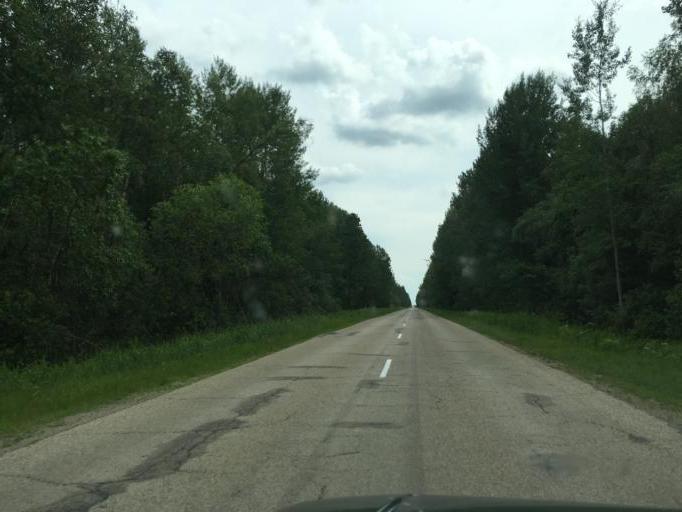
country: LV
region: Rugaju
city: Rugaji
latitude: 56.7915
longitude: 27.1009
